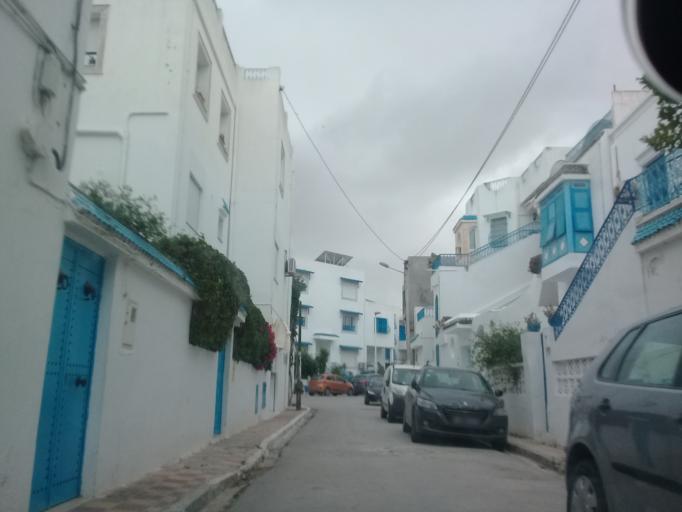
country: TN
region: Tunis
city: Sidi Bou Said
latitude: 36.8714
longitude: 10.3385
